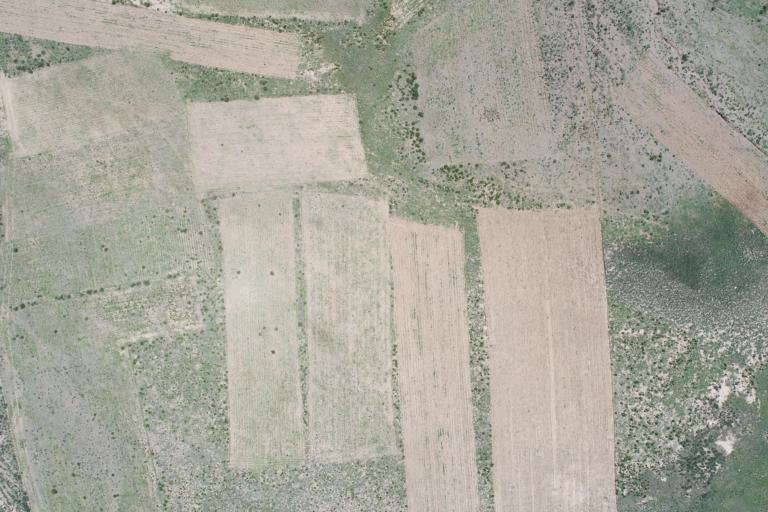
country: BO
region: La Paz
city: Curahuara de Carangas
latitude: -17.3225
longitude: -68.5145
